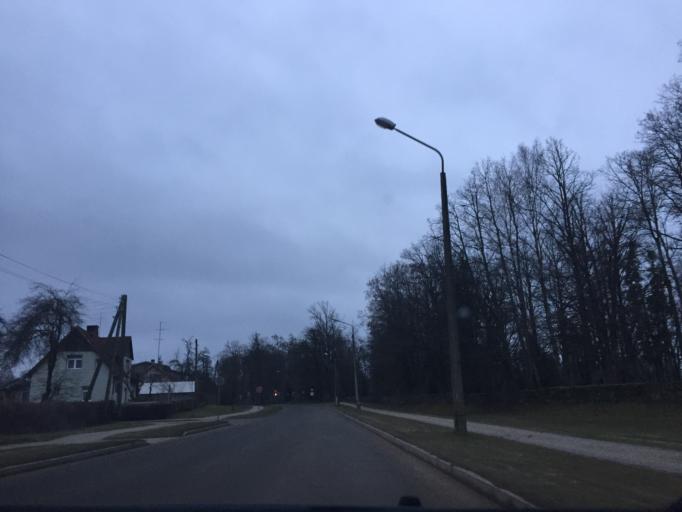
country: LV
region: Cesu Rajons
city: Cesis
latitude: 57.3180
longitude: 25.2673
